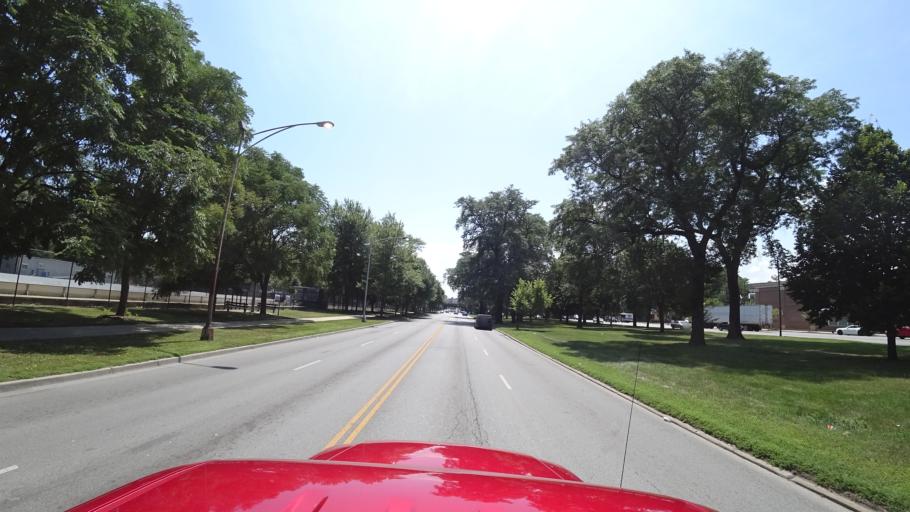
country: US
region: Illinois
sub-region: Cook County
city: Chicago
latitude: 41.8254
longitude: -87.6843
